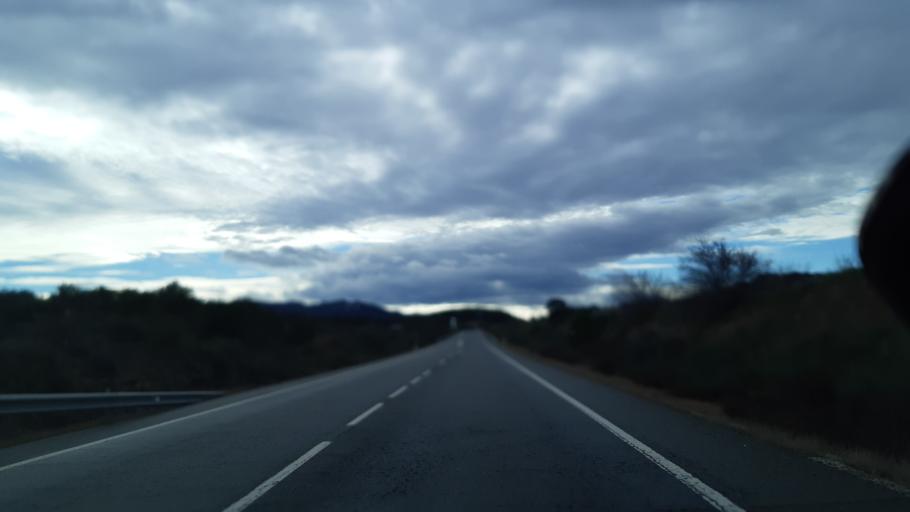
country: ES
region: Catalonia
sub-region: Provincia de Tarragona
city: la Fatarella
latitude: 41.1073
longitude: 0.5285
